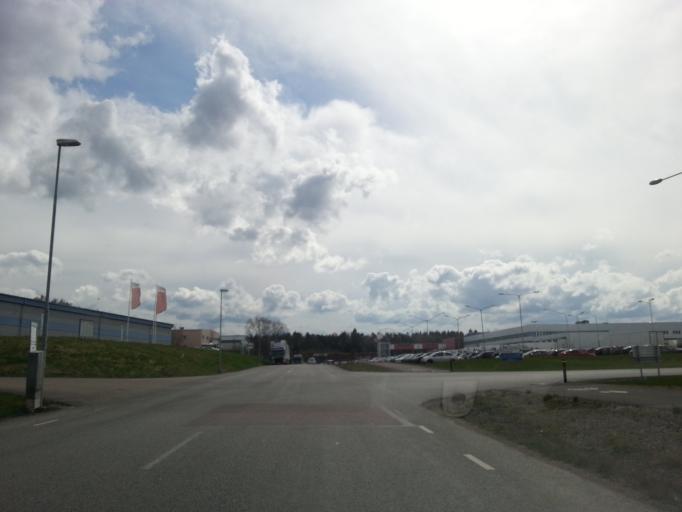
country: SE
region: Vaestra Goetaland
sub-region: Kungalvs Kommun
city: Kungalv
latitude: 57.8767
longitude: 11.9315
